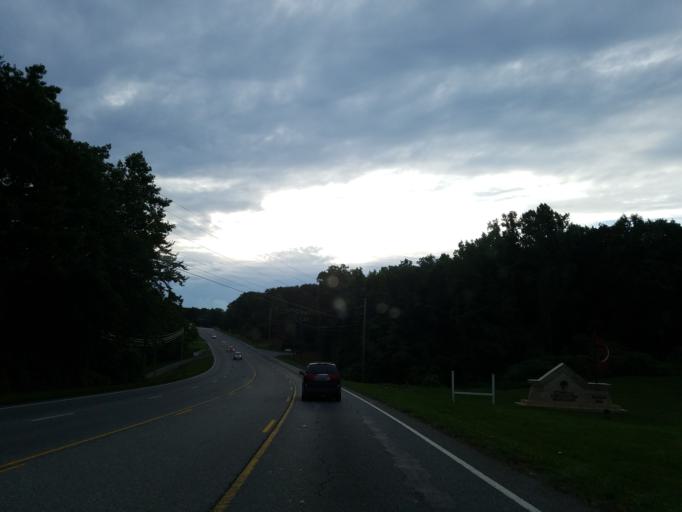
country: US
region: Georgia
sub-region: Forsyth County
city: Cumming
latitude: 34.2257
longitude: -84.1585
